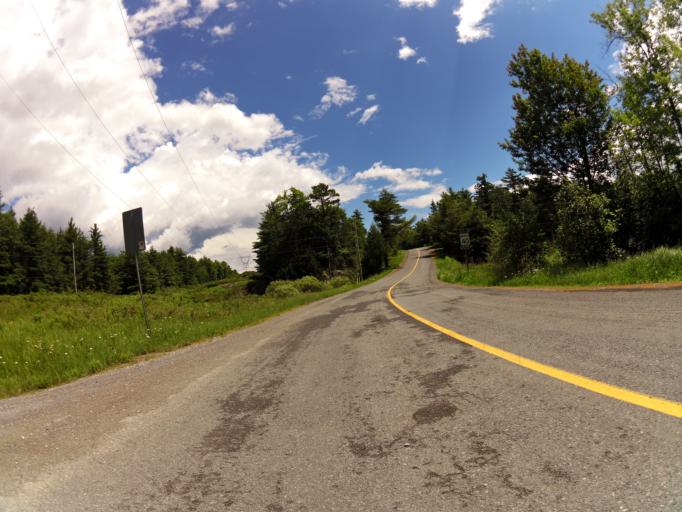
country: CA
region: Ontario
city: Renfrew
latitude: 45.0604
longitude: -76.6628
